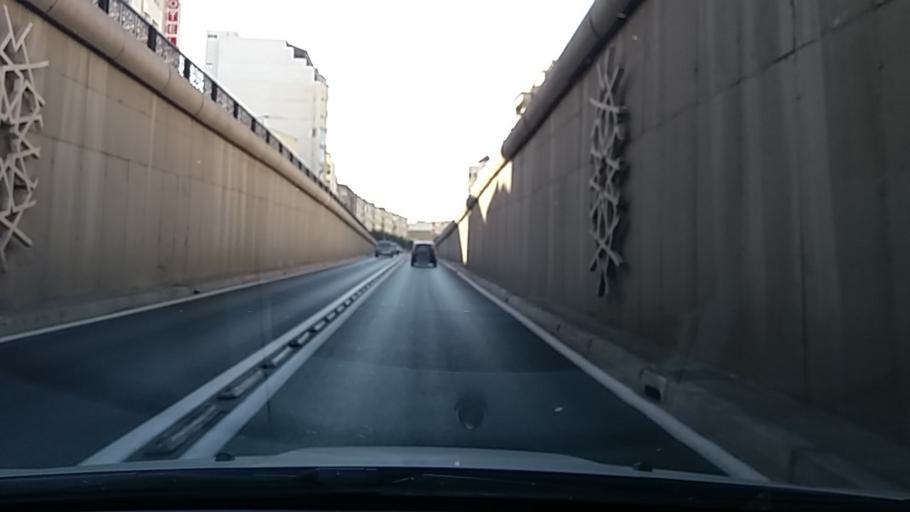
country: MA
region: Tanger-Tetouan
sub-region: Tanger-Assilah
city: Tangier
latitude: 35.7721
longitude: -5.8147
